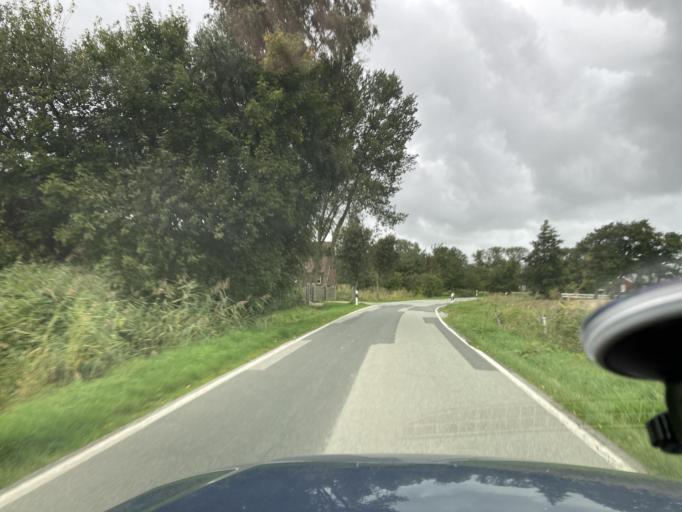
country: DE
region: Schleswig-Holstein
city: Norderwohrden
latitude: 54.1987
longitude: 8.9993
